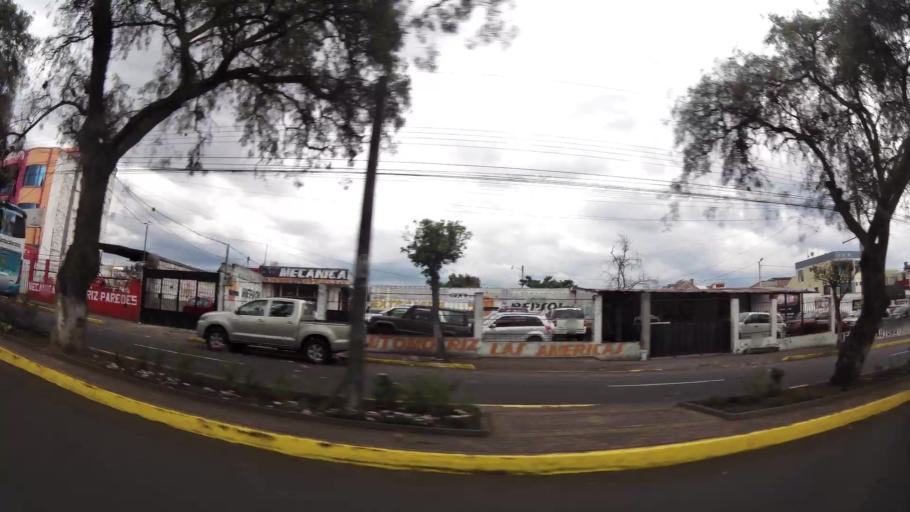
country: EC
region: Tungurahua
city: Ambato
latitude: -1.2324
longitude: -78.6142
